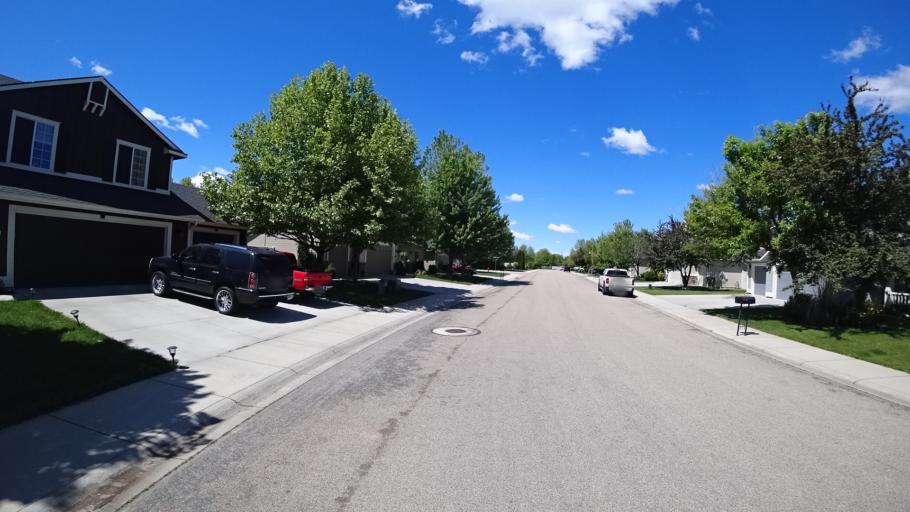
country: US
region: Idaho
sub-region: Ada County
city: Meridian
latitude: 43.6286
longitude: -116.3418
